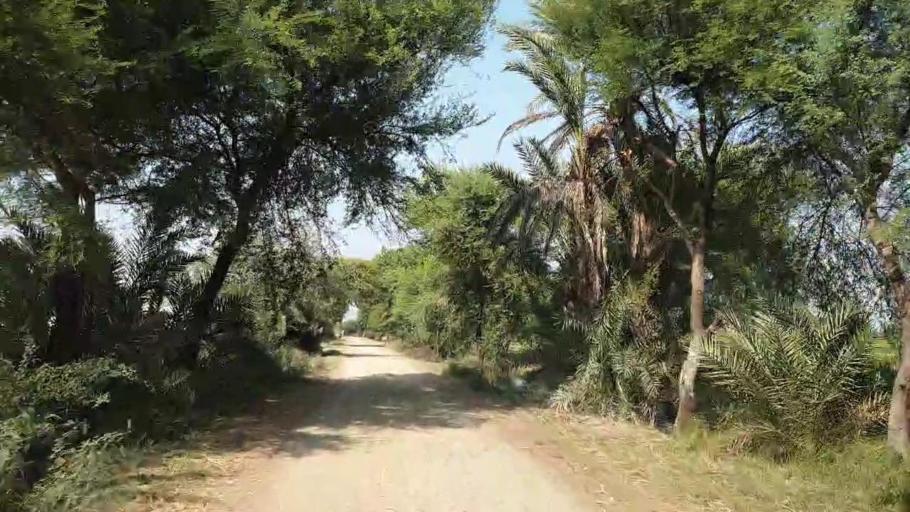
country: PK
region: Sindh
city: Tando Muhammad Khan
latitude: 25.0280
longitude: 68.4079
